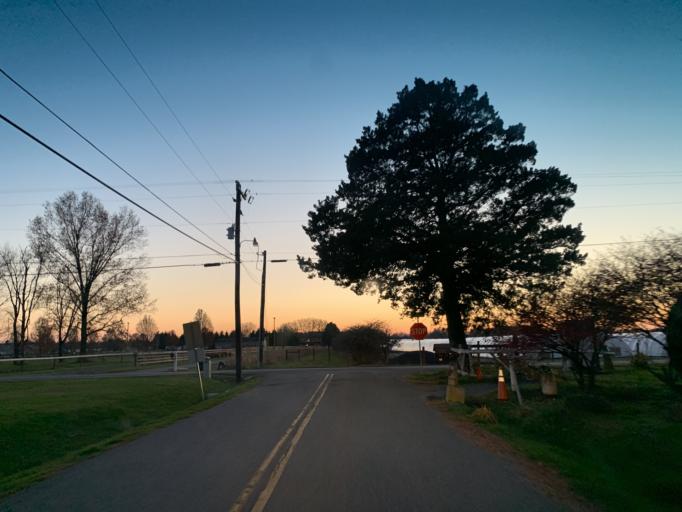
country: US
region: Delaware
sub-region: New Castle County
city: Middletown
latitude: 39.4202
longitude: -75.7816
